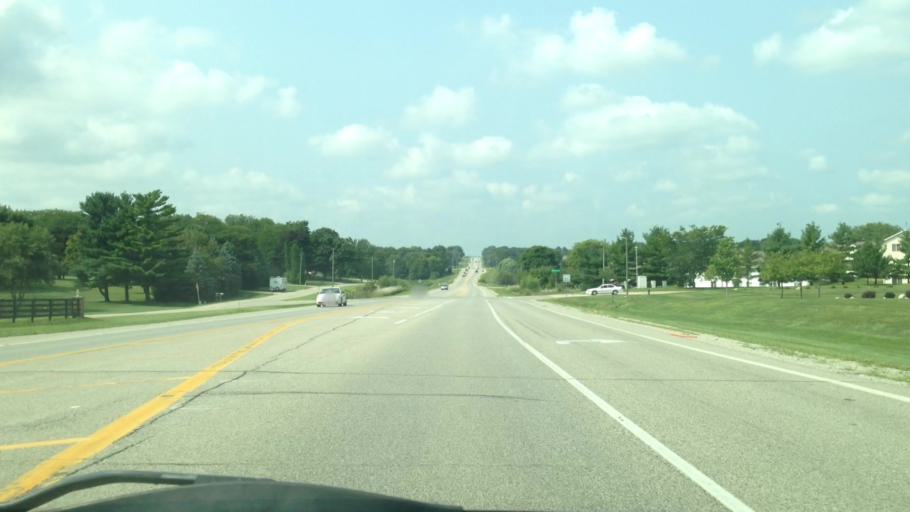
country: US
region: Iowa
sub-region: Linn County
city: Fairfax
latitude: 41.9429
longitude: -91.7464
